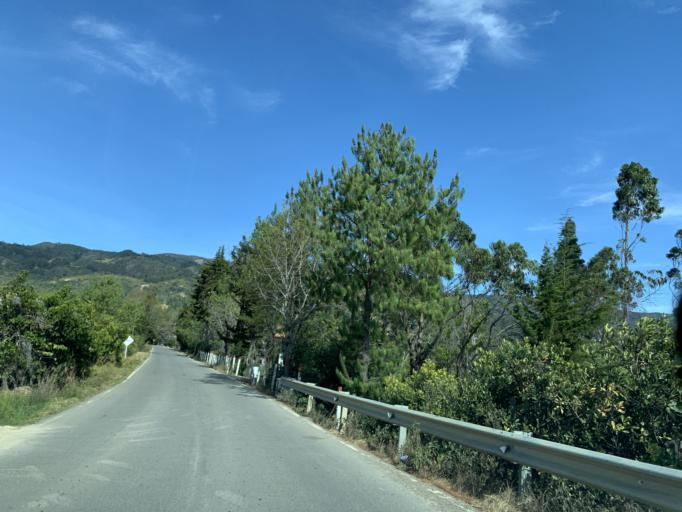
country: CO
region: Boyaca
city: Santa Sofia
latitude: 5.7069
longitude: -73.5969
